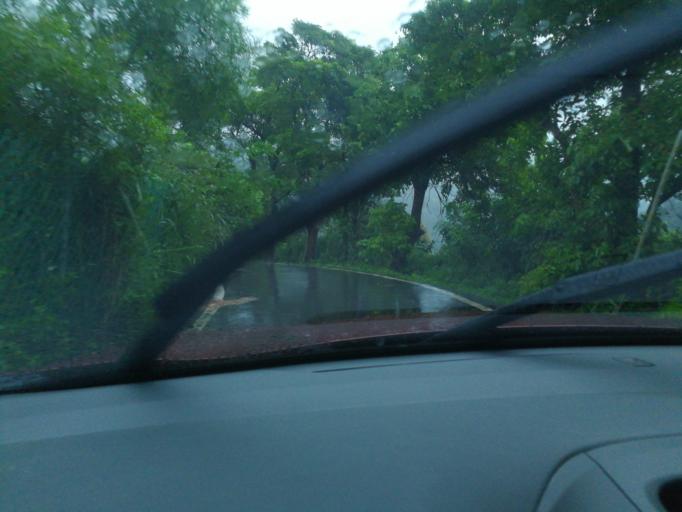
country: TW
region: Taipei
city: Taipei
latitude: 25.1110
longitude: 121.6245
